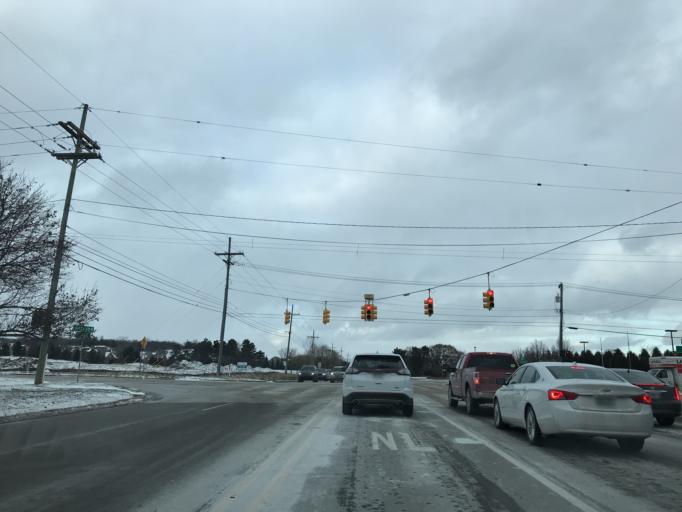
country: US
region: Michigan
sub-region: Wayne County
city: Plymouth
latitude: 42.3953
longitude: -83.4816
